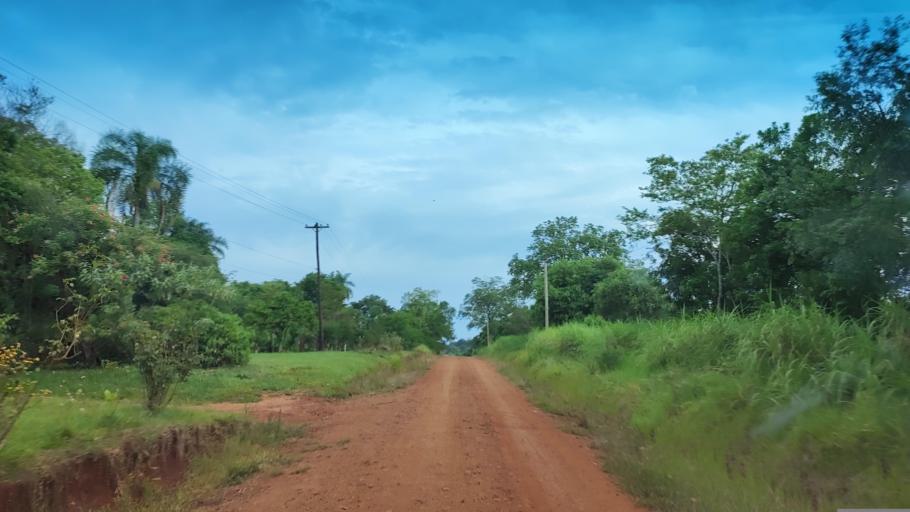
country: AR
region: Misiones
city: Gobernador Roca
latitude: -27.1542
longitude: -55.4681
